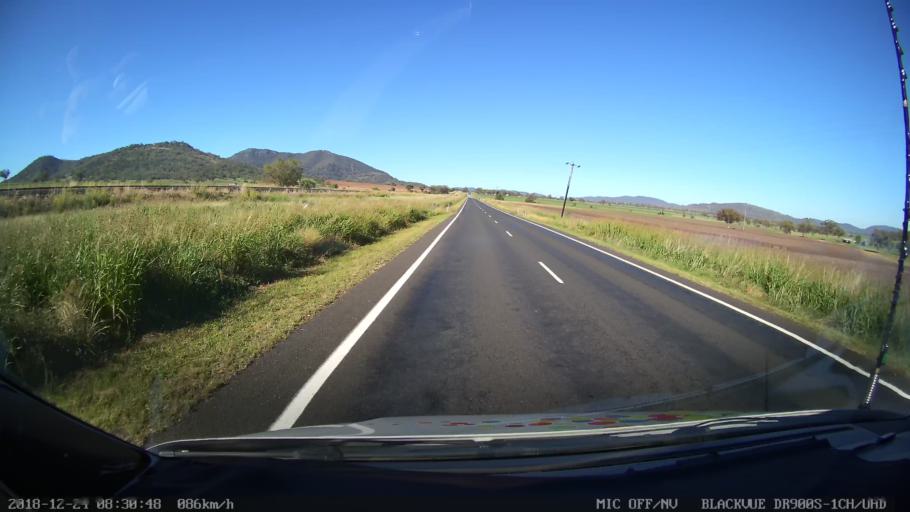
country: AU
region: New South Wales
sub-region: Tamworth Municipality
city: Phillip
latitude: -31.2696
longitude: 150.7200
